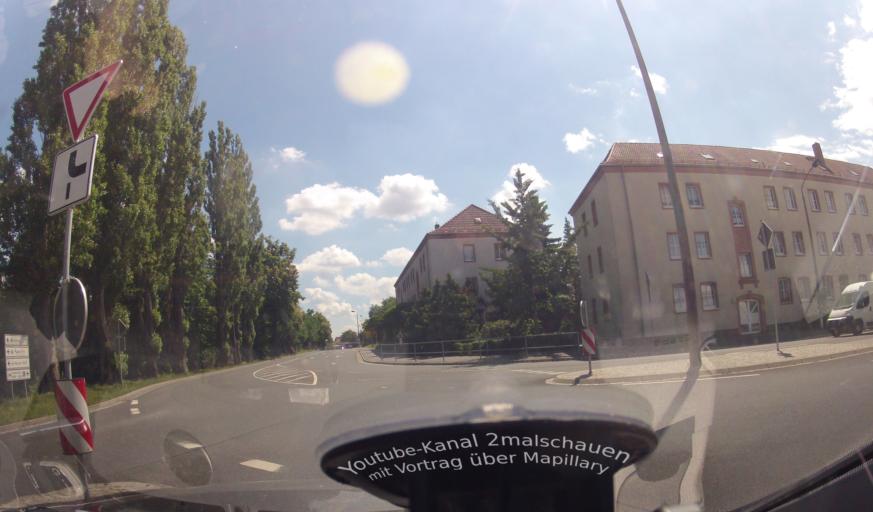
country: DE
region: Saxony
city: Torgau
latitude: 51.5588
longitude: 12.9927
